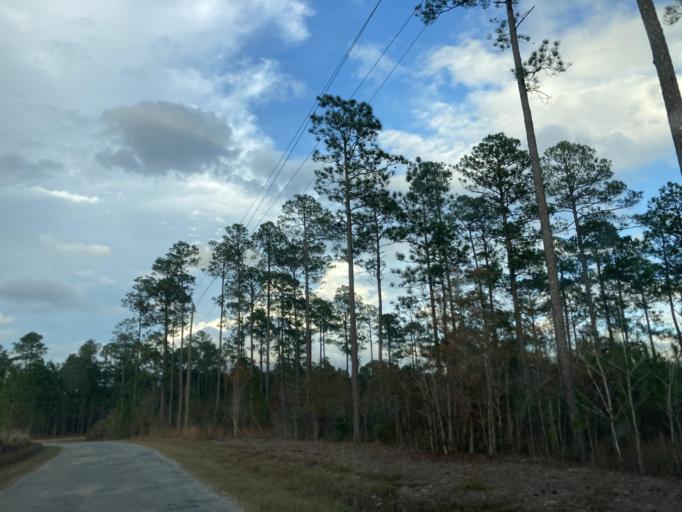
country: US
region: Mississippi
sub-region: Lamar County
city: Purvis
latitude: 31.1957
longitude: -89.6004
